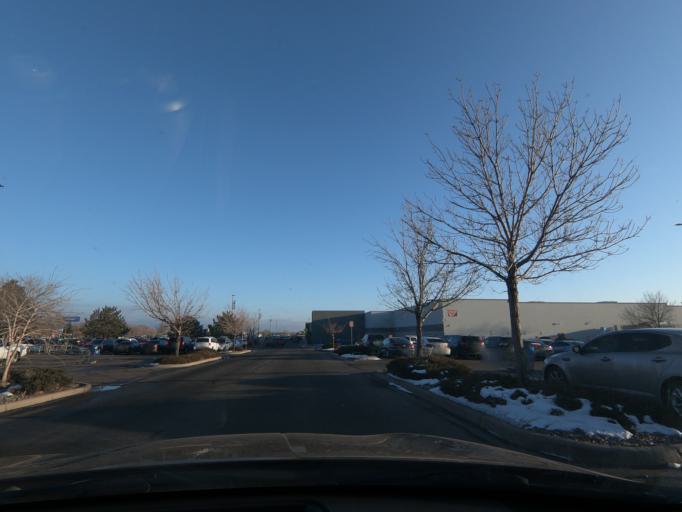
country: US
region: Colorado
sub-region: El Paso County
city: Security-Widefield
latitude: 38.7417
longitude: -104.7371
